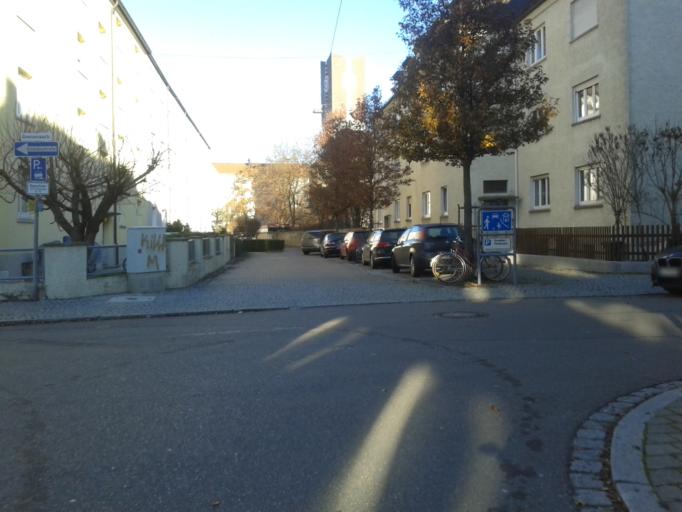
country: DE
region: Baden-Wuerttemberg
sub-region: Tuebingen Region
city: Ulm
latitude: 48.3944
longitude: 9.9733
